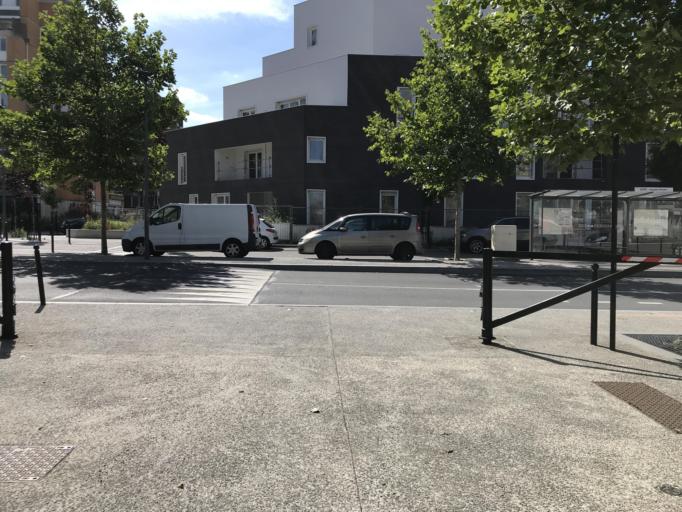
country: FR
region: Ile-de-France
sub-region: Departement de l'Essonne
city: Evry
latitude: 48.6340
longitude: 2.4297
